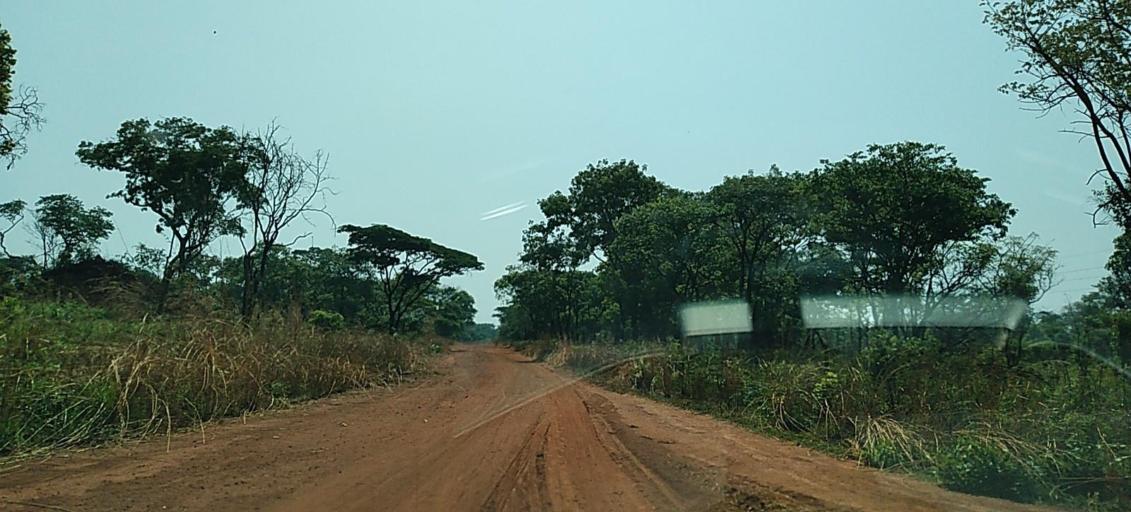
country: ZM
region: North-Western
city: Kansanshi
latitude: -12.0083
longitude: 26.5163
